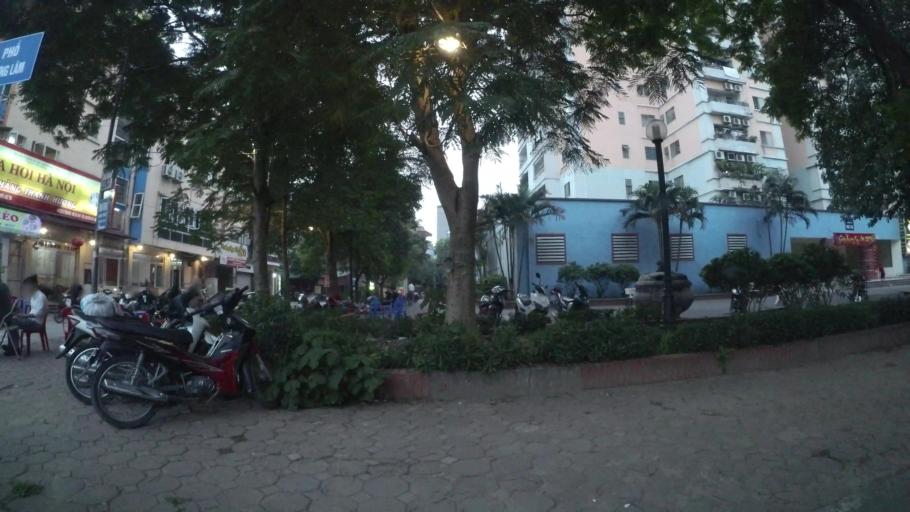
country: VN
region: Ha Noi
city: Ha Dong
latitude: 20.9721
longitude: 105.7901
